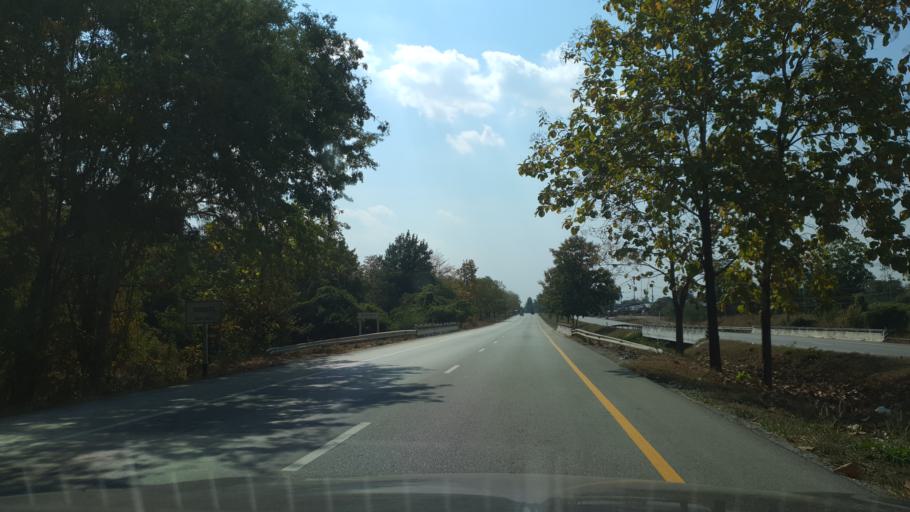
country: TH
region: Tak
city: Sam Ngao
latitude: 17.3012
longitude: 99.1462
